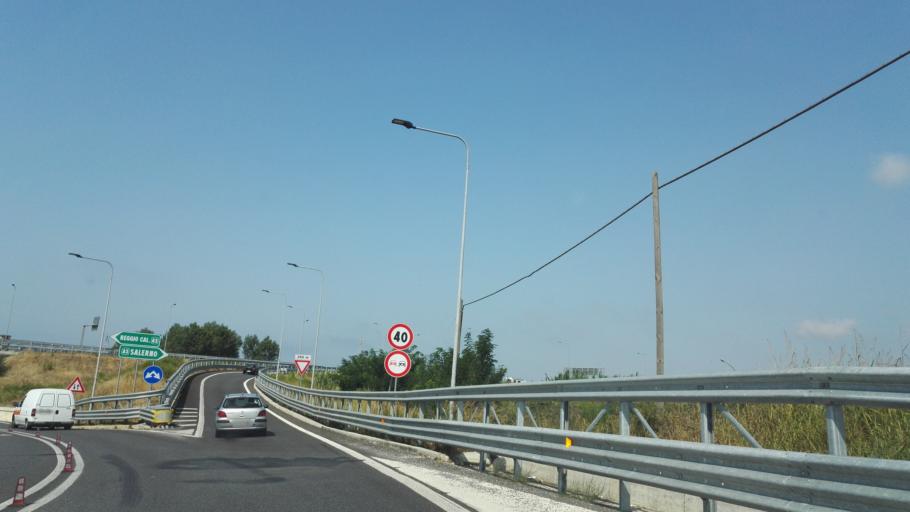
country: IT
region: Calabria
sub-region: Provincia di Catanzaro
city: Santa Eufemia Lamezia
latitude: 38.9189
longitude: 16.2663
